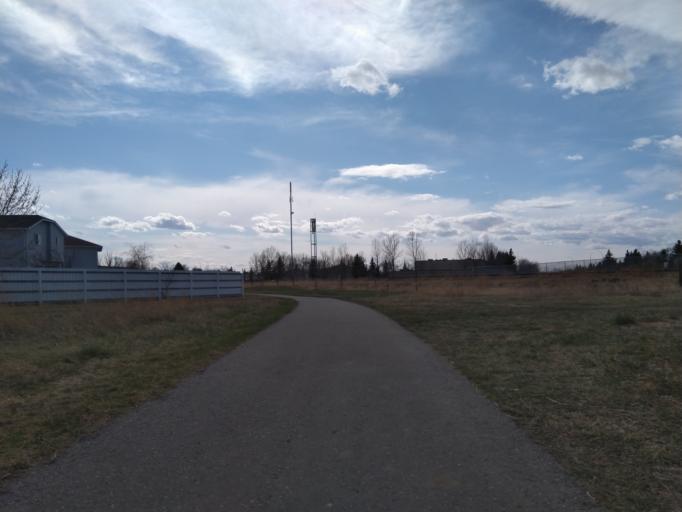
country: CA
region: Alberta
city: Chestermere
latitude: 51.0524
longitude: -113.9265
